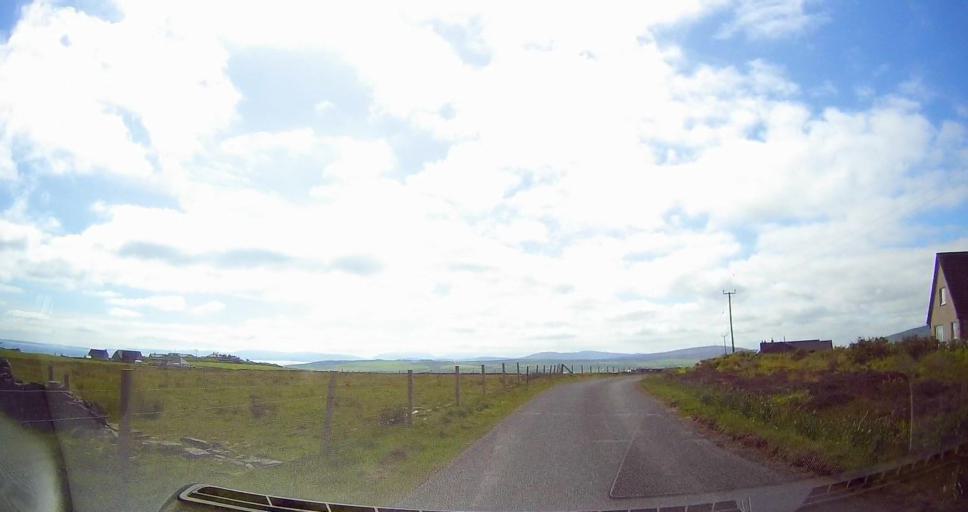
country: GB
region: Scotland
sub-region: Orkney Islands
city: Kirkwall
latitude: 58.9628
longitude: -2.9535
